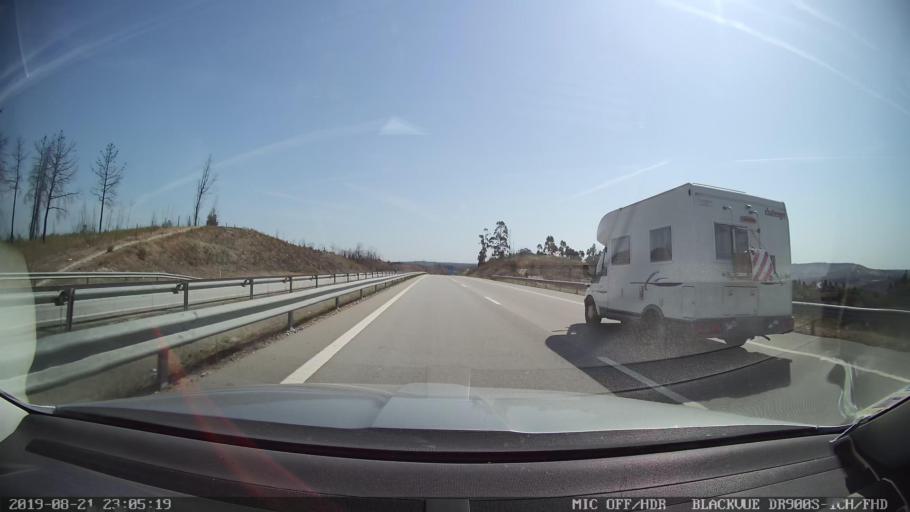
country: PT
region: Portalegre
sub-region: Gaviao
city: Gaviao
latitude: 39.5508
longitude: -7.8141
